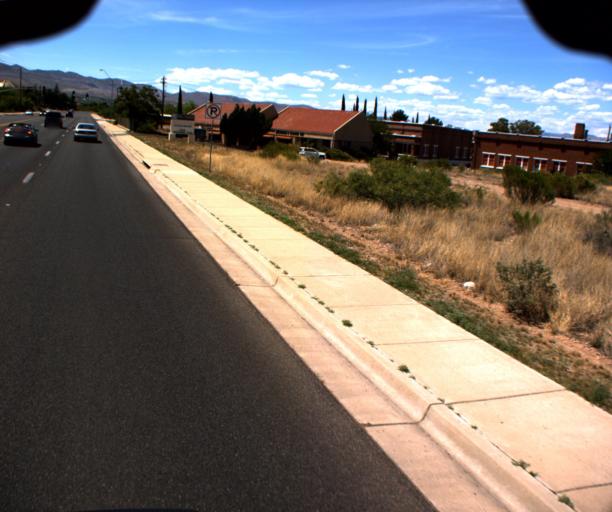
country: US
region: Arizona
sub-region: Yavapai County
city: Cottonwood
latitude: 34.7315
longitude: -112.0262
